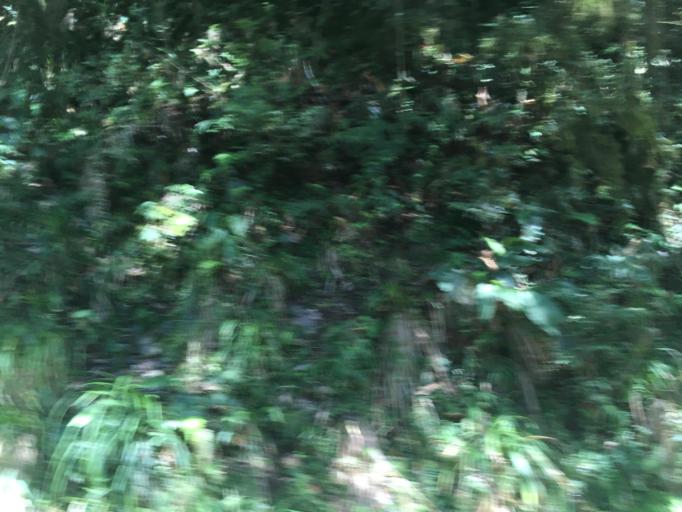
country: TW
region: Taiwan
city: Daxi
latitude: 24.6106
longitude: 121.4599
